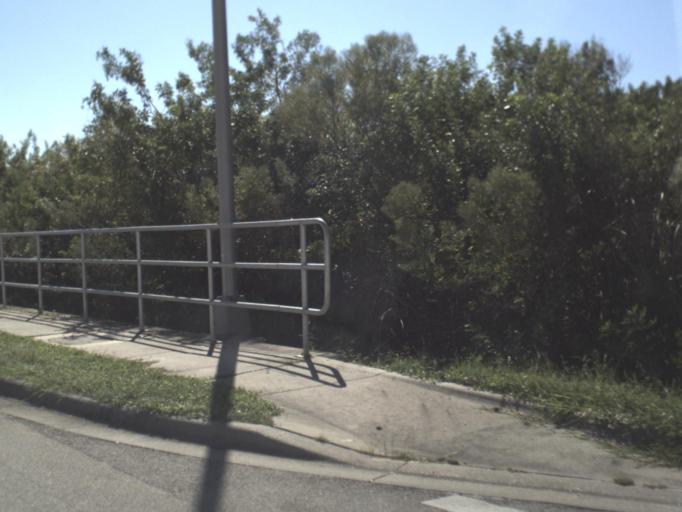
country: US
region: Florida
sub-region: Sarasota County
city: North Port
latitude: 26.9647
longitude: -82.2112
